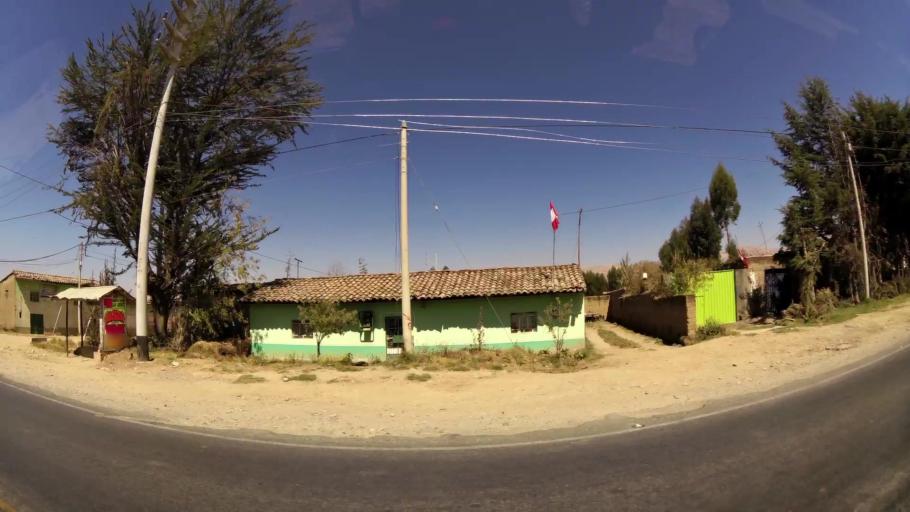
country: PE
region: Junin
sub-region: Provincia de Concepcion
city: Matahuasi
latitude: -11.8792
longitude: -75.3586
